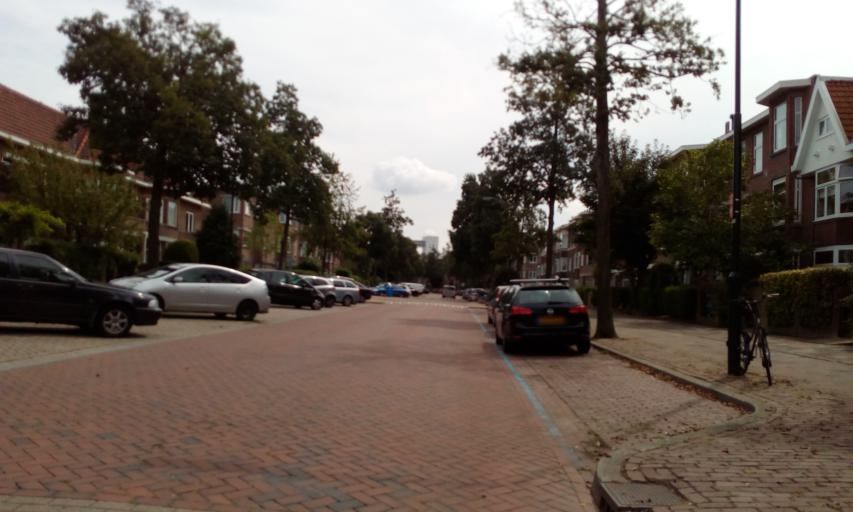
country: NL
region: South Holland
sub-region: Gemeente Leidschendam-Voorburg
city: Voorburg
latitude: 52.0738
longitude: 4.3458
